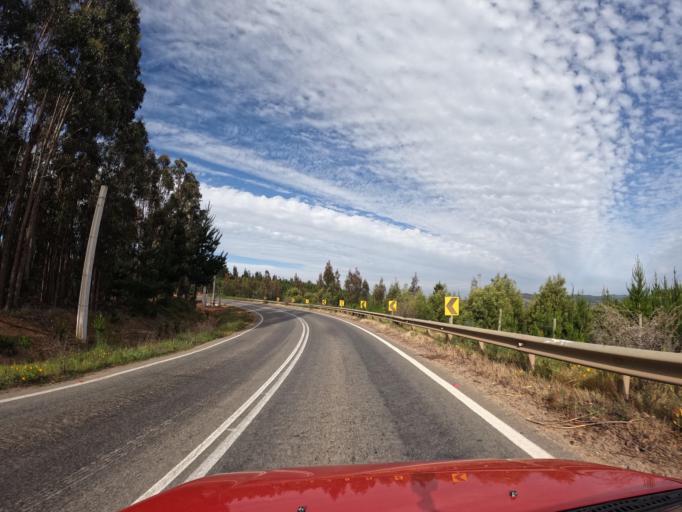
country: CL
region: O'Higgins
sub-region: Provincia de Colchagua
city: Santa Cruz
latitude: -34.3039
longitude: -71.8300
